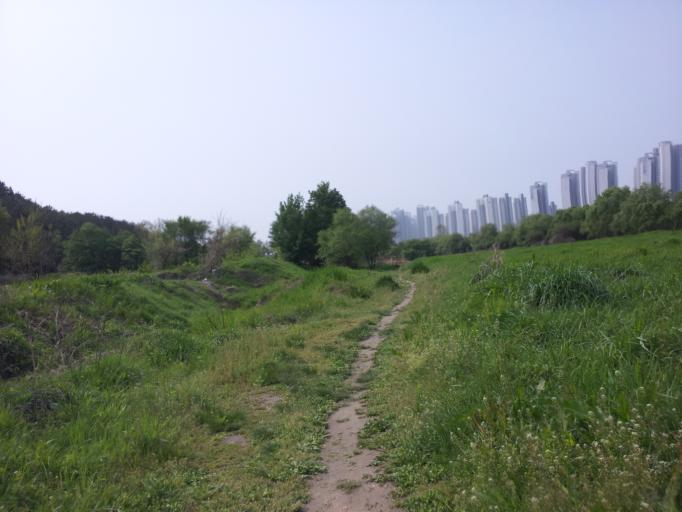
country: KR
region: Daejeon
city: Daejeon
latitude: 36.3228
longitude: 127.3534
